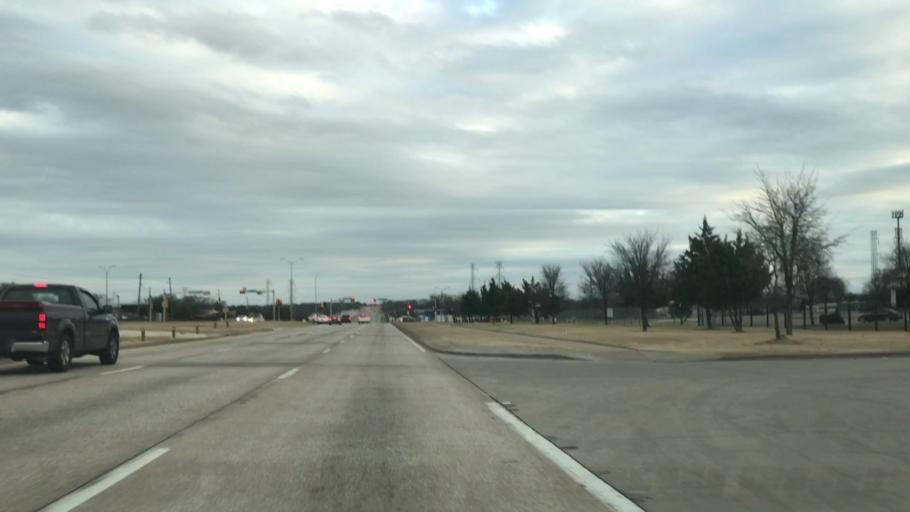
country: US
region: Texas
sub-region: Dallas County
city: Cockrell Hill
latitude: 32.7126
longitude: -96.9100
